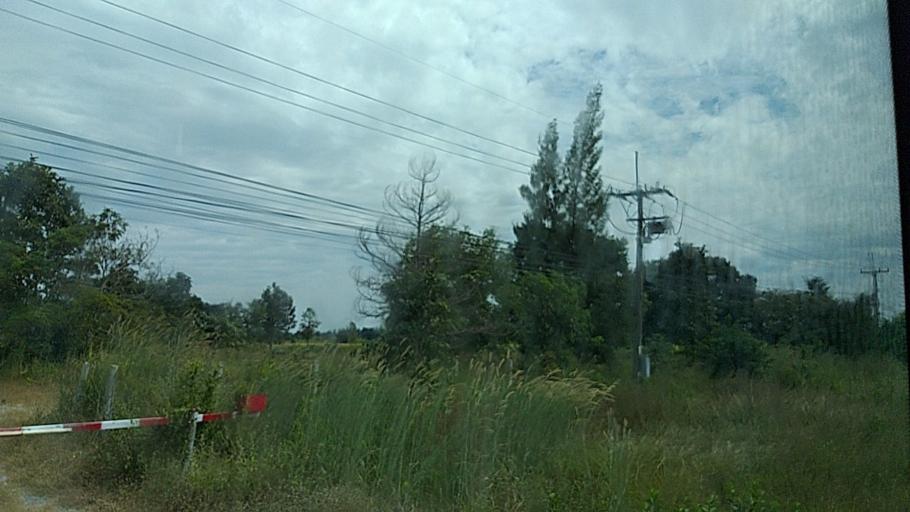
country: TH
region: Maha Sarakham
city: Chiang Yuen
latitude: 16.3597
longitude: 103.1117
